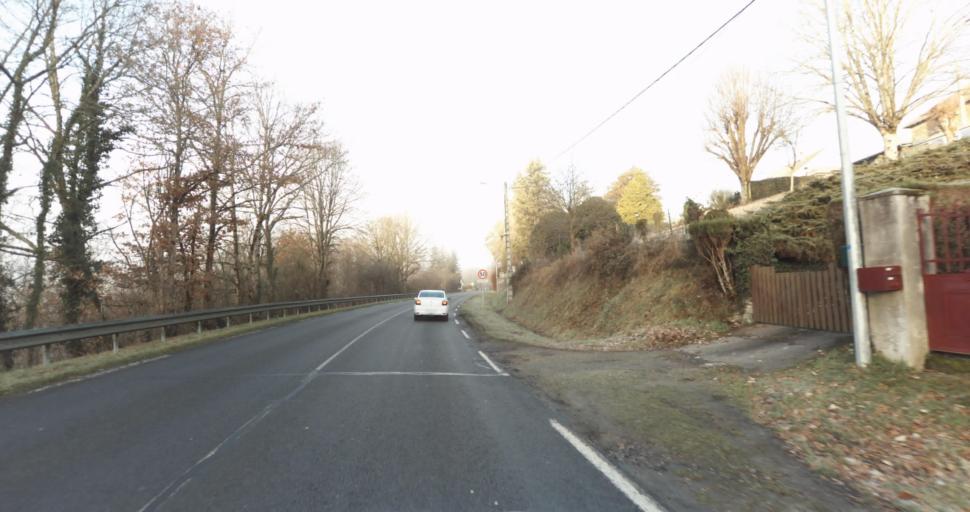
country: FR
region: Limousin
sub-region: Departement de la Haute-Vienne
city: Aixe-sur-Vienne
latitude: 45.7914
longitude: 1.1580
